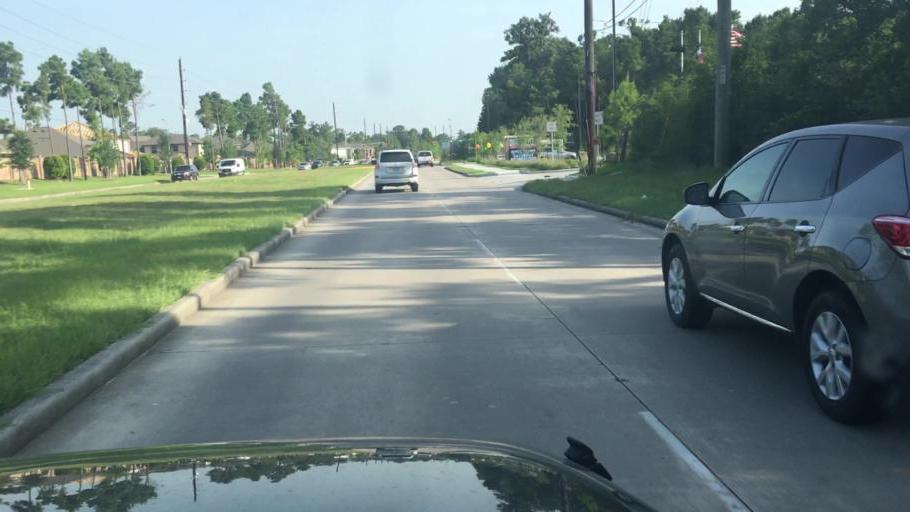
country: US
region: Texas
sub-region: Harris County
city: Atascocita
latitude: 29.9405
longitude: -95.1758
